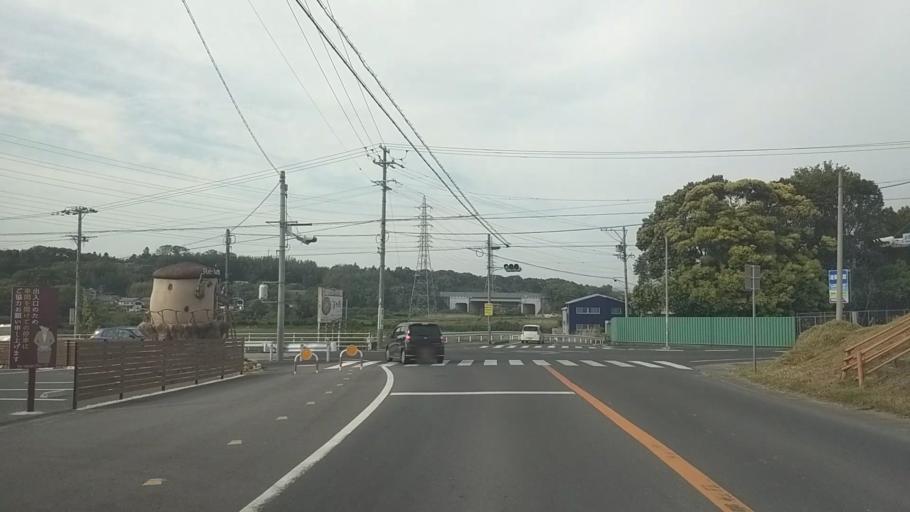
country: JP
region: Shizuoka
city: Hamamatsu
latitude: 34.7613
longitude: 137.6608
